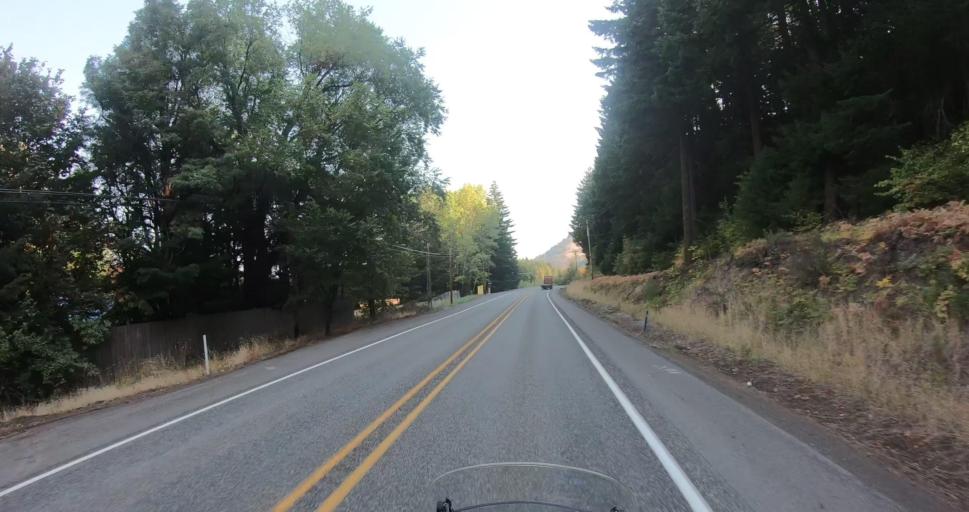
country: US
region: Washington
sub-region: Klickitat County
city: White Salmon
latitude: 45.7719
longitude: -121.5221
